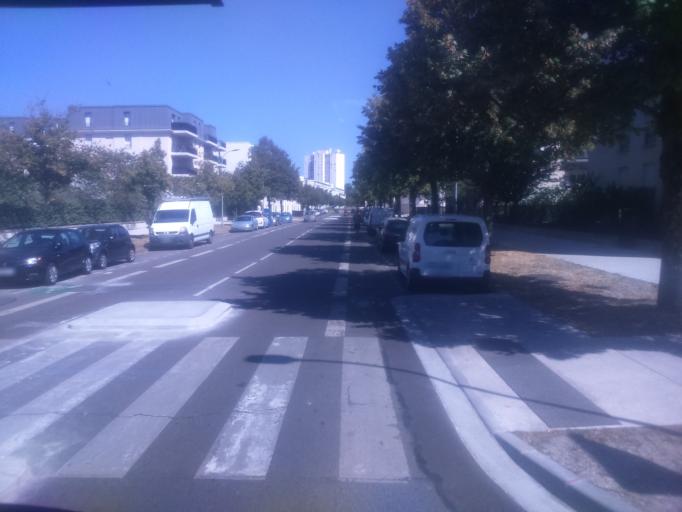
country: FR
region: Aquitaine
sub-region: Departement de la Gironde
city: Le Bouscat
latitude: 44.8648
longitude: -0.5707
